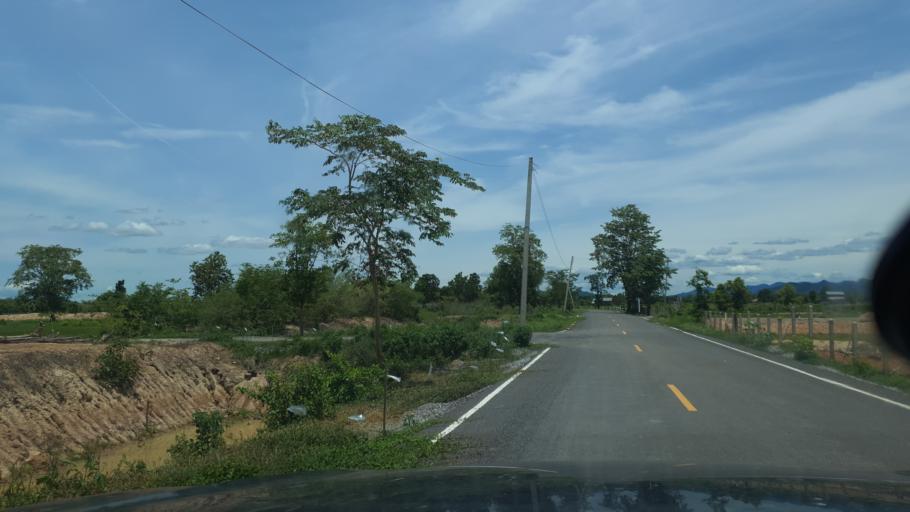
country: TH
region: Sukhothai
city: Ban Dan Lan Hoi
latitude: 17.1507
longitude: 99.6409
